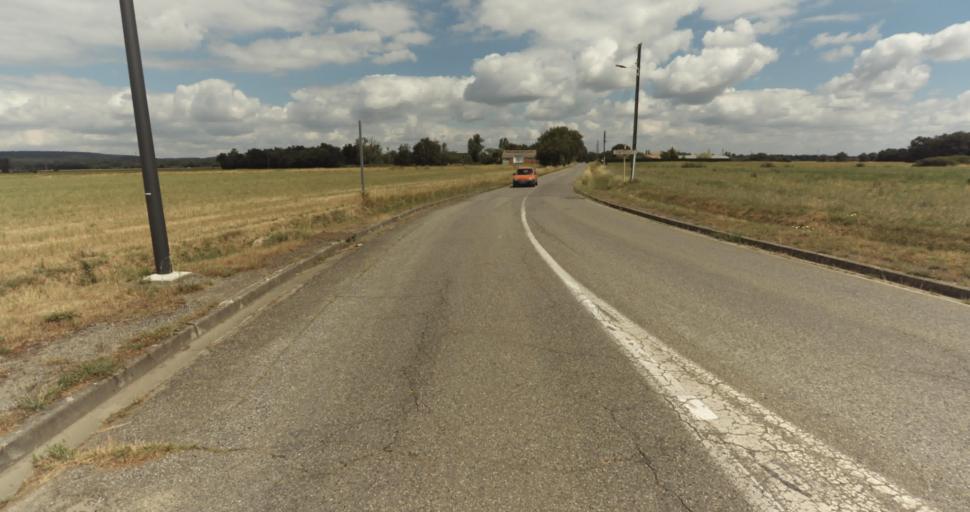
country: FR
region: Midi-Pyrenees
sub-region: Departement de la Haute-Garonne
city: Fontenilles
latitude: 43.5584
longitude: 1.1932
